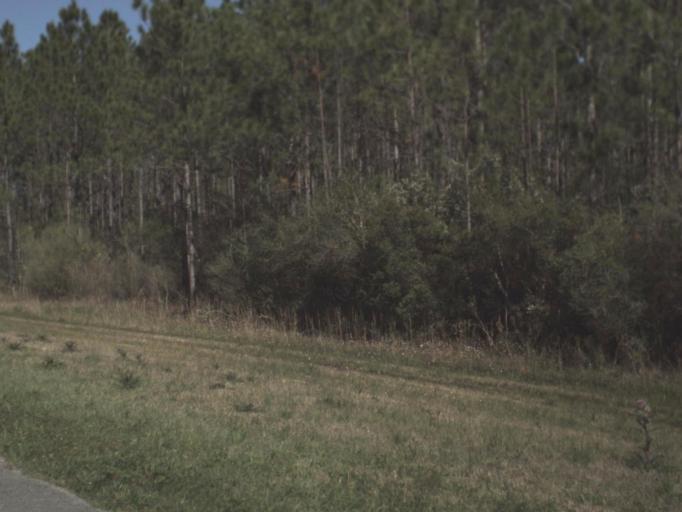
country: US
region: Florida
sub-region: Gulf County
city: Port Saint Joe
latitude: 29.9091
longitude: -85.2058
